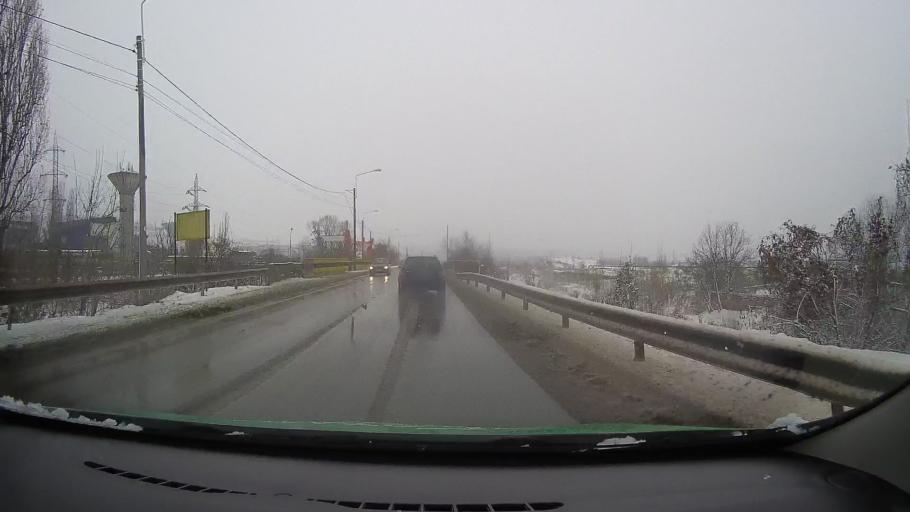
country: RO
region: Hunedoara
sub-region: Municipiul Hunedoara
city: Pestisu Mare
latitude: 45.7840
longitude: 22.9110
